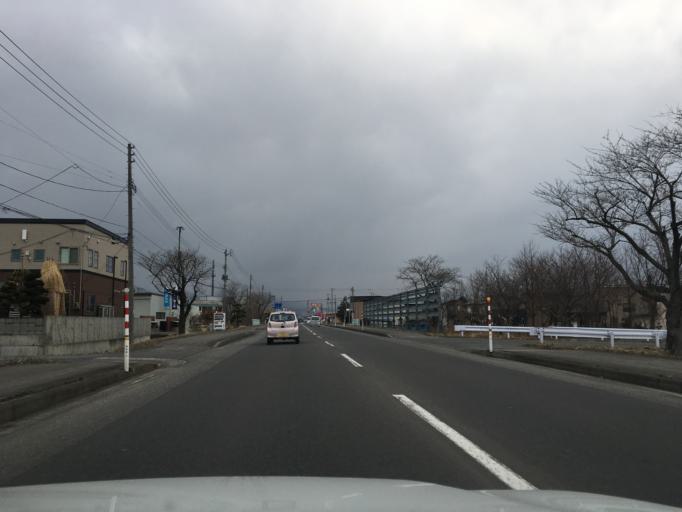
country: JP
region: Aomori
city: Kuroishi
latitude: 40.5889
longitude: 140.5690
